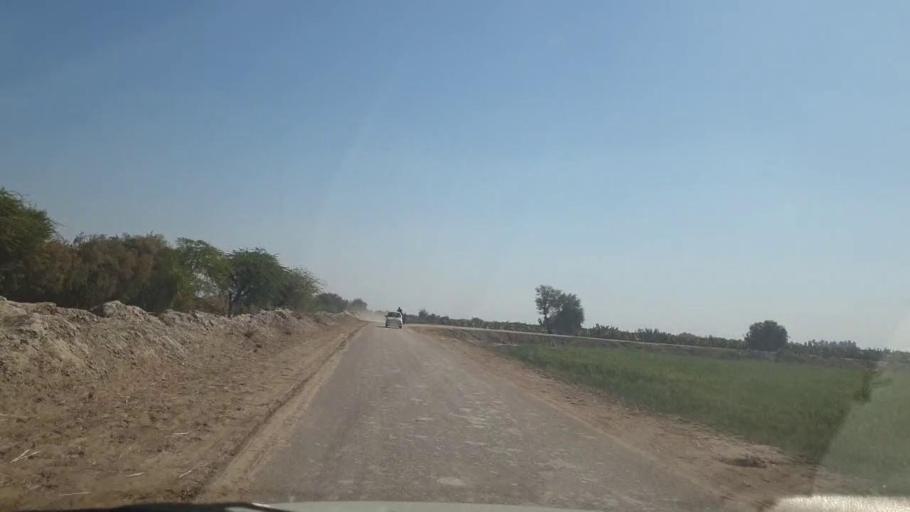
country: PK
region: Sindh
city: Mirpur Khas
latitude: 25.4611
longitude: 69.1809
